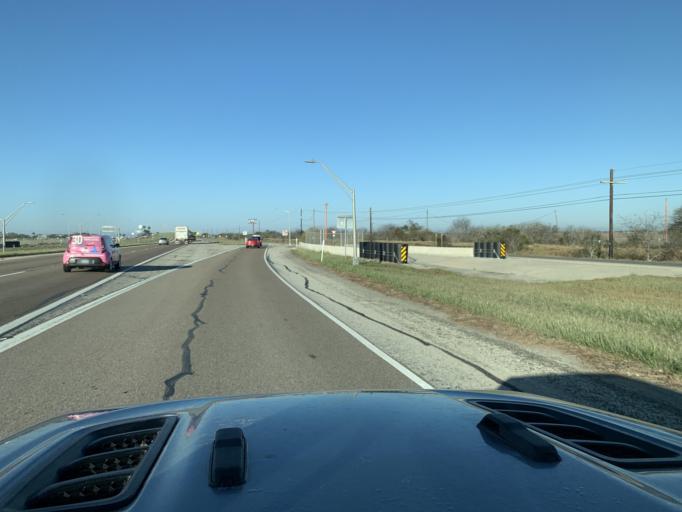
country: US
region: Texas
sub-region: Nueces County
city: Corpus Christi
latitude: 27.7851
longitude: -97.4956
